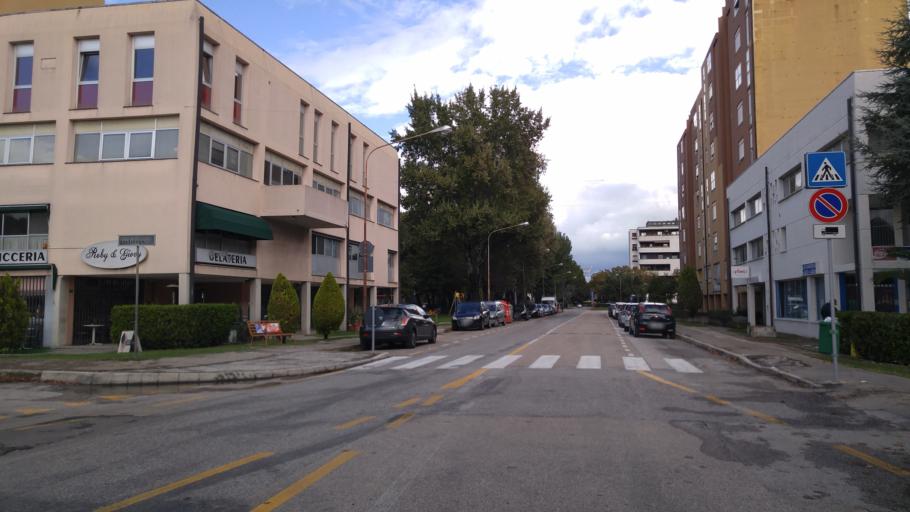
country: IT
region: The Marches
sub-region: Provincia di Pesaro e Urbino
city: Pesaro
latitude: 43.8954
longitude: 12.8984
